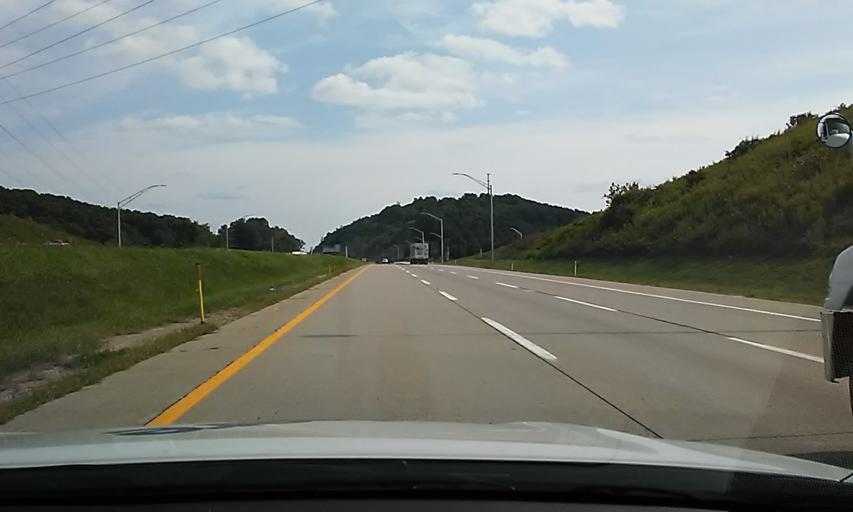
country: US
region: Pennsylvania
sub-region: Westmoreland County
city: Delmont
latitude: 40.3838
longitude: -79.5679
